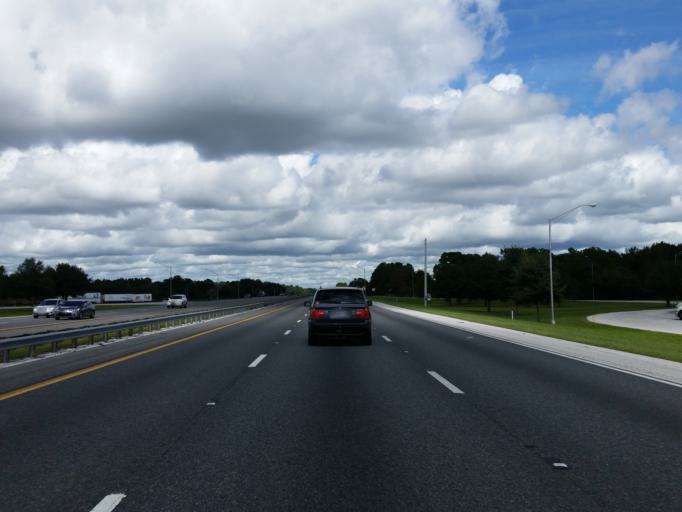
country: US
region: Florida
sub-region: Marion County
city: Ocala
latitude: 29.0931
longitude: -82.1849
